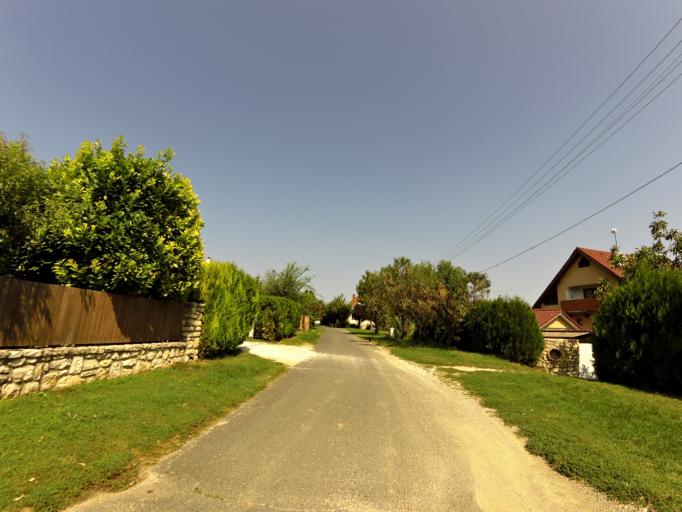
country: HU
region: Zala
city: Vonyarcvashegy
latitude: 46.8021
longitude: 17.3767
